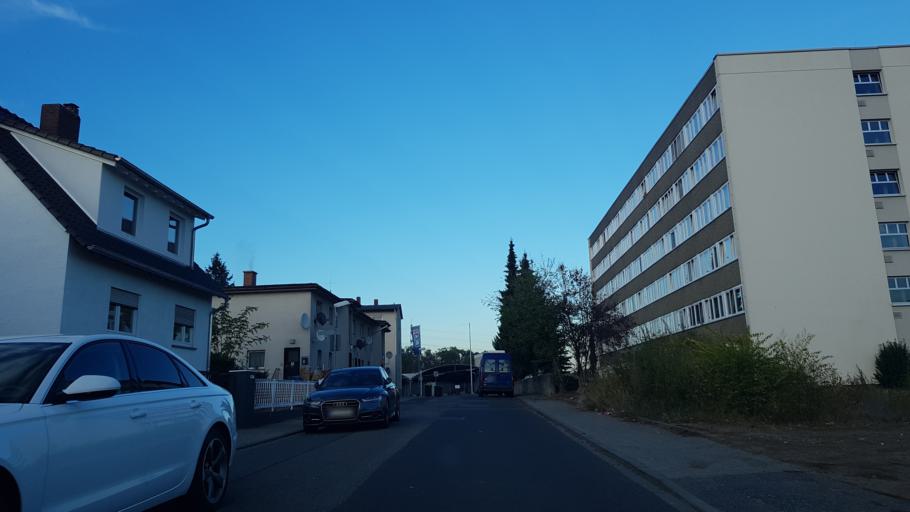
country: DE
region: Hesse
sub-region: Regierungsbezirk Darmstadt
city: Gross-Gerau
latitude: 49.9345
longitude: 8.4893
